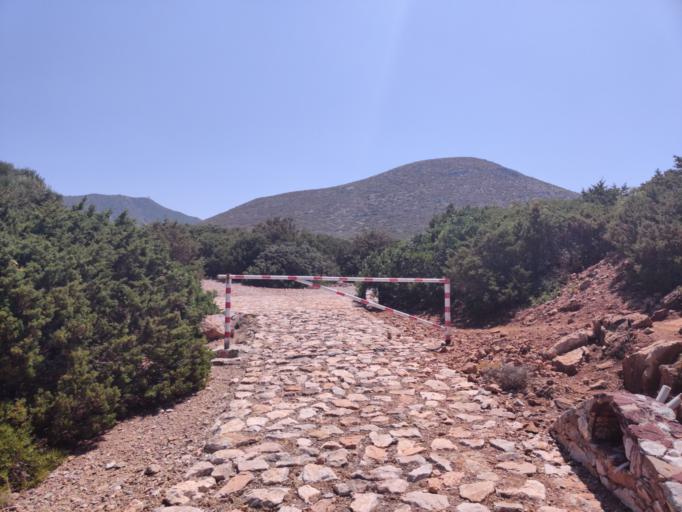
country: IT
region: Sardinia
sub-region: Provincia di Carbonia-Iglesias
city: Buggerru
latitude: 39.3933
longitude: 8.3909
